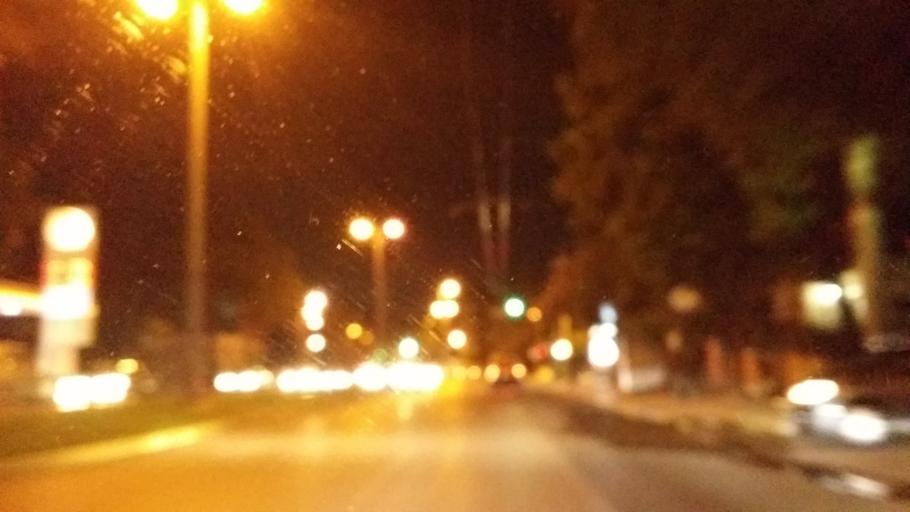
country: GR
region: Attica
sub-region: Nomarchia Athinas
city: Khalandrion
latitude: 38.0205
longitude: 23.7939
